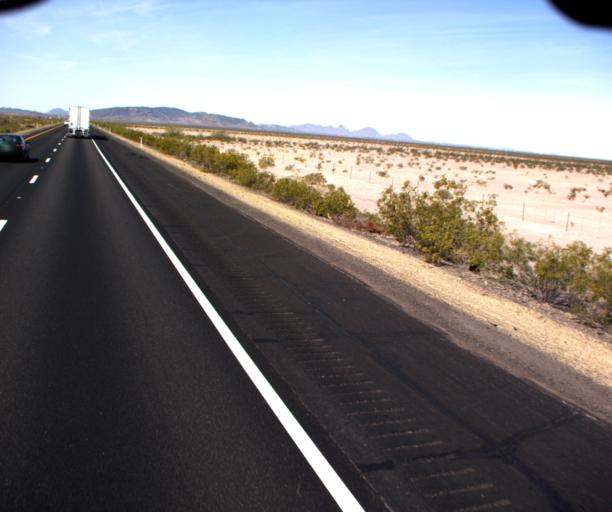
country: US
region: Arizona
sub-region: La Paz County
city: Salome
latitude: 33.6351
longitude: -113.7935
